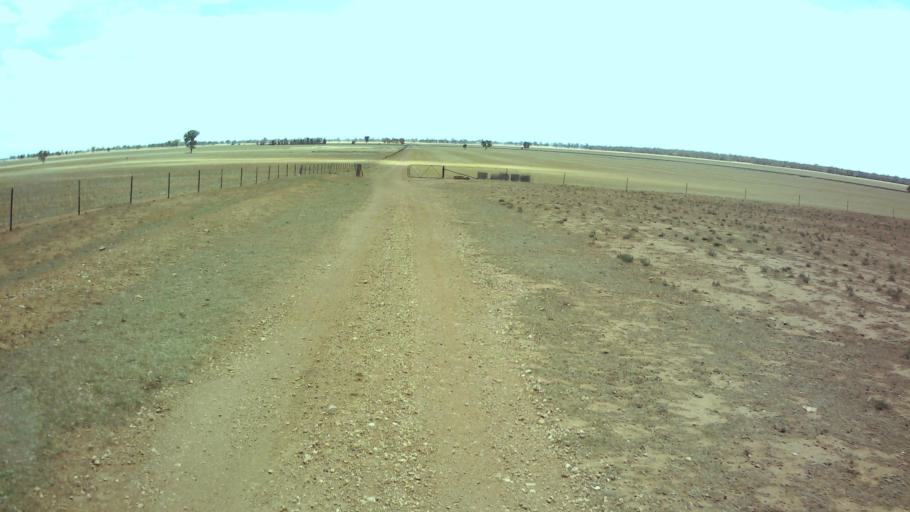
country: AU
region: New South Wales
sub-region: Weddin
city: Grenfell
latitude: -33.9036
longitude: 147.7384
